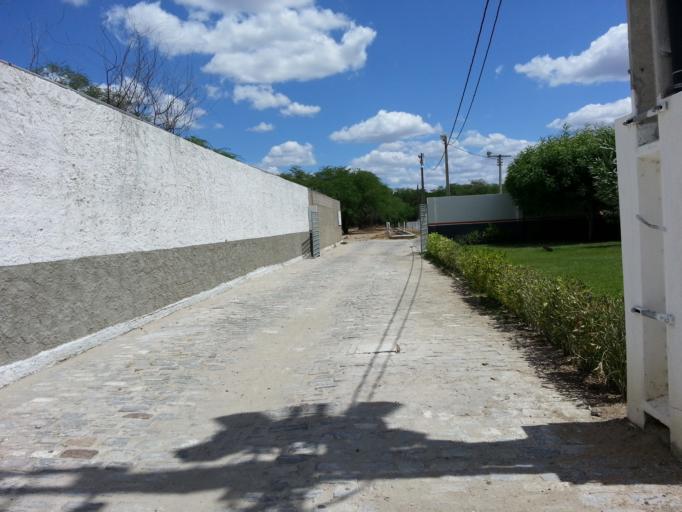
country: BR
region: Ceara
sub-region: Quixada
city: Quixada
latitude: -4.9756
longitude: -39.0145
